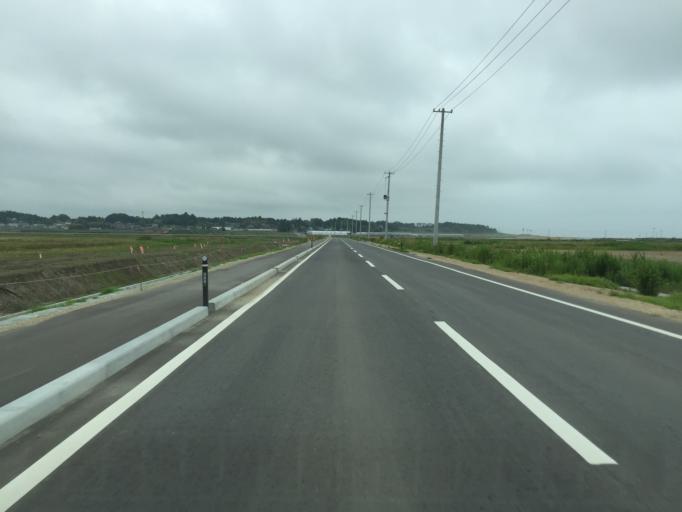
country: JP
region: Fukushima
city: Namie
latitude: 37.6975
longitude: 141.0058
